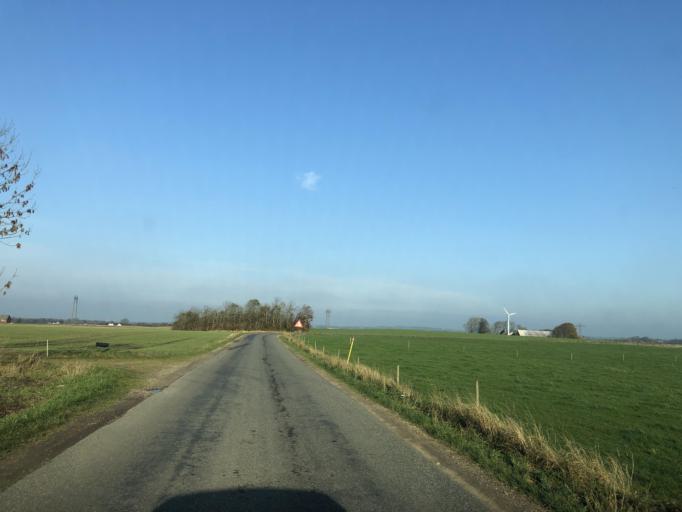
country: DK
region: Central Jutland
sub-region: Holstebro Kommune
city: Vinderup
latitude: 56.3908
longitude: 8.7319
